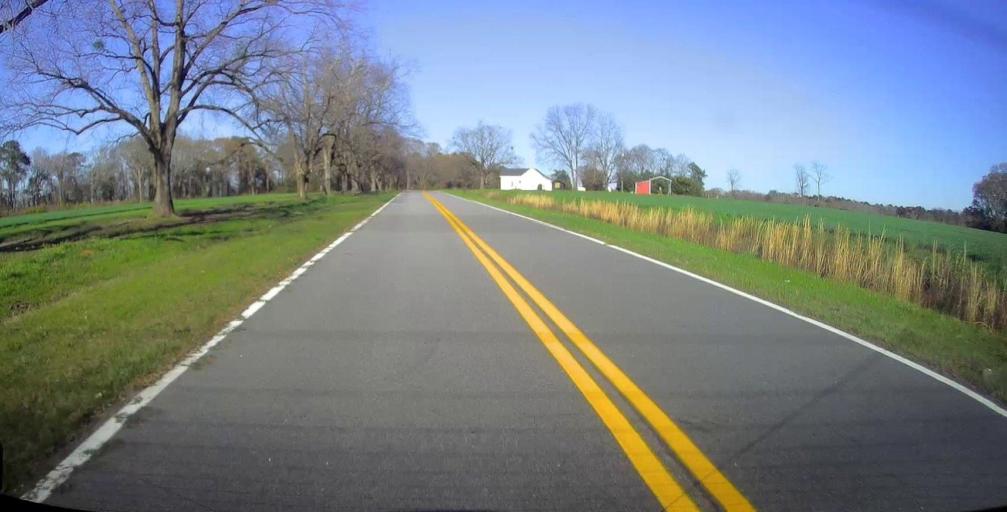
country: US
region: Georgia
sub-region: Peach County
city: Byron
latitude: 32.6737
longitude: -83.8215
